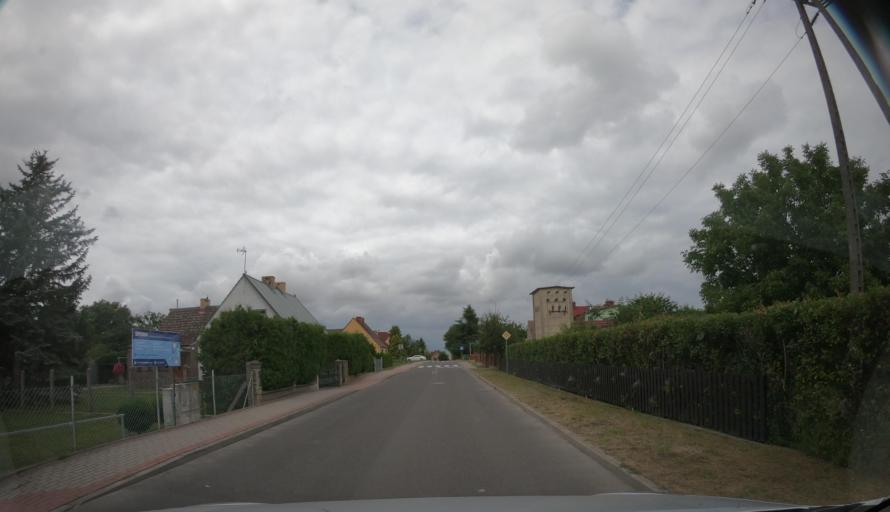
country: PL
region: West Pomeranian Voivodeship
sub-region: Powiat kamienski
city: Golczewo
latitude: 53.8196
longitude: 14.9831
